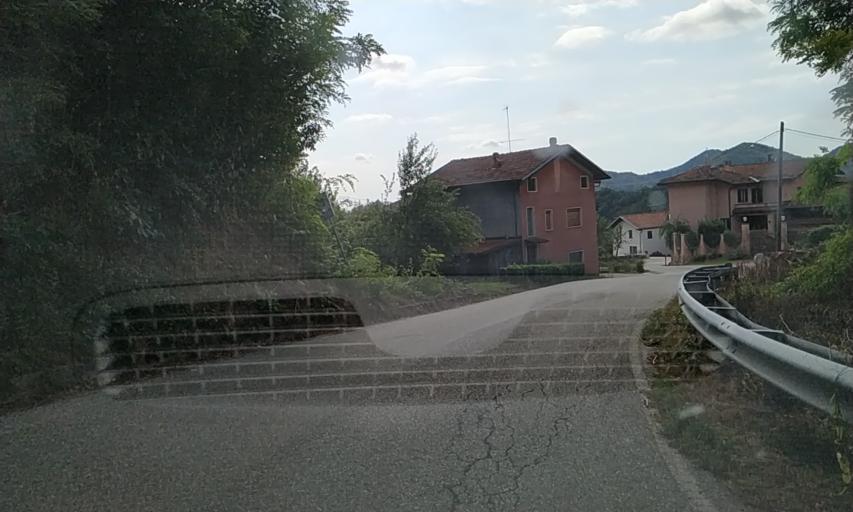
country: IT
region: Piedmont
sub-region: Provincia di Biella
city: Frazione Chiesa
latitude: 45.6908
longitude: 8.2154
